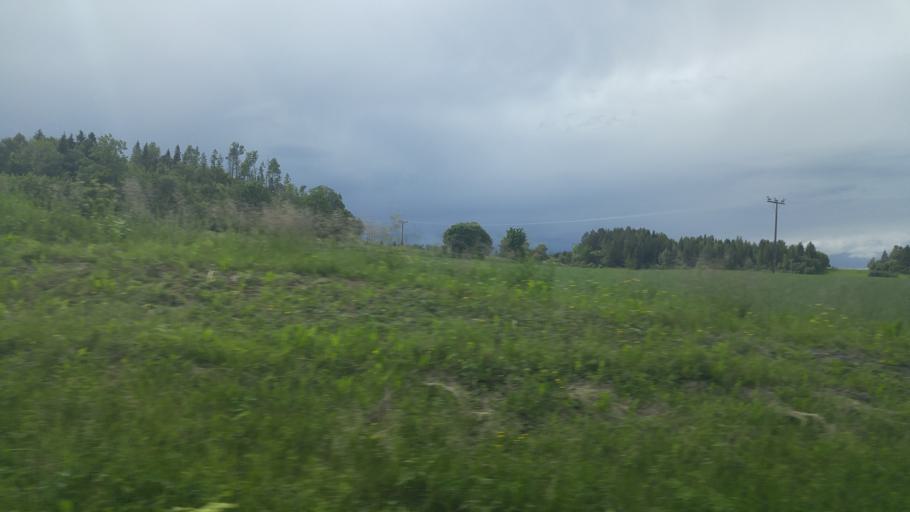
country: NO
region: Nord-Trondelag
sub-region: Stjordal
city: Stjordal
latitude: 63.5165
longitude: 10.8581
